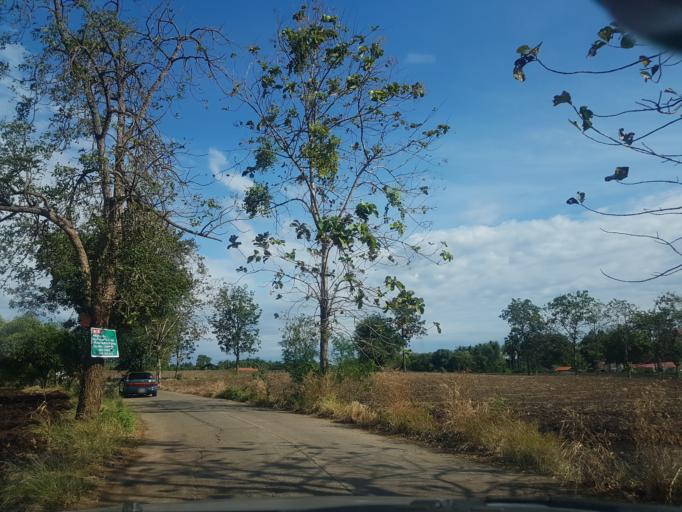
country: TH
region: Sara Buri
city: Phra Phutthabat
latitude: 14.8269
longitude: 100.7634
